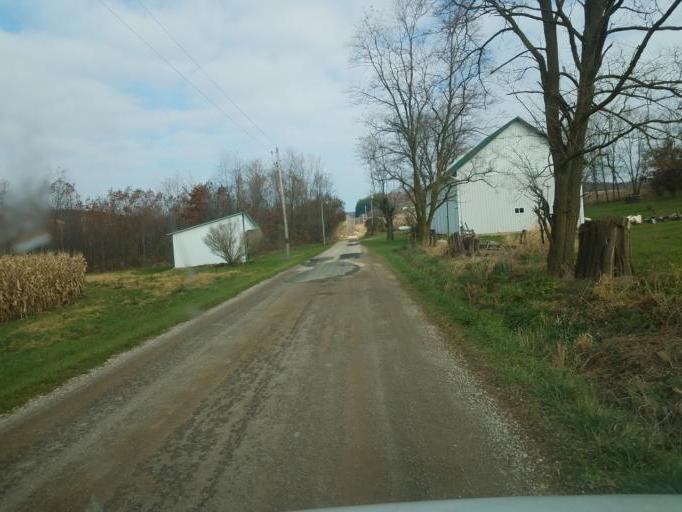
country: US
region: Ohio
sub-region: Knox County
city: Danville
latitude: 40.5320
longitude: -82.2811
